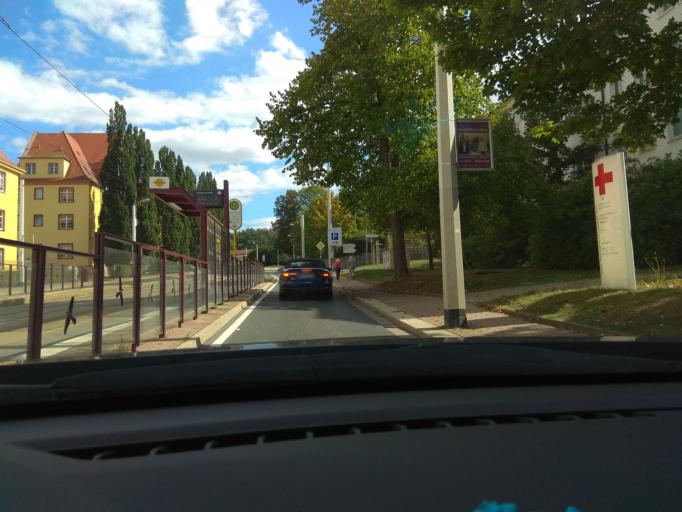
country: DE
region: Saxony
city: Plauen
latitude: 50.4915
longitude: 12.1559
